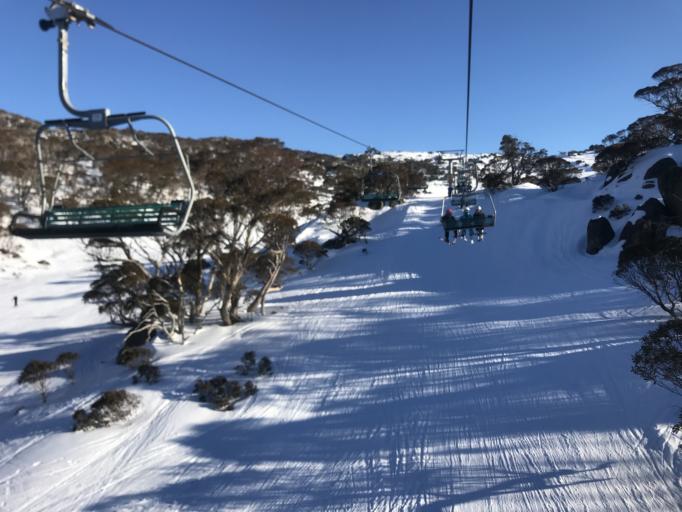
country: AU
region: New South Wales
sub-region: Snowy River
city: Jindabyne
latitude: -36.3879
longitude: 148.3986
